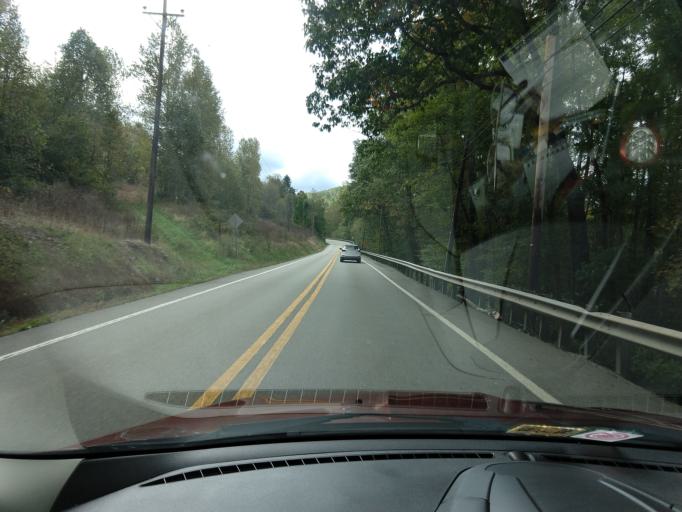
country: US
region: West Virginia
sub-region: Barbour County
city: Belington
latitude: 39.0072
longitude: -79.9397
